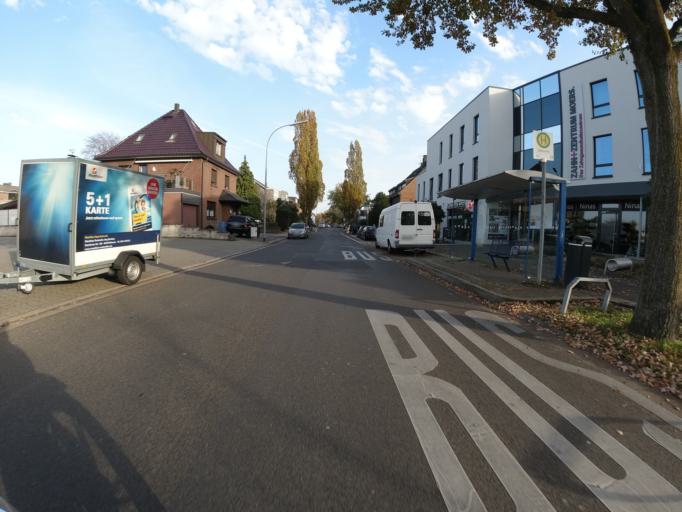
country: DE
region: North Rhine-Westphalia
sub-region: Regierungsbezirk Dusseldorf
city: Moers
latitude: 51.4257
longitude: 6.6591
